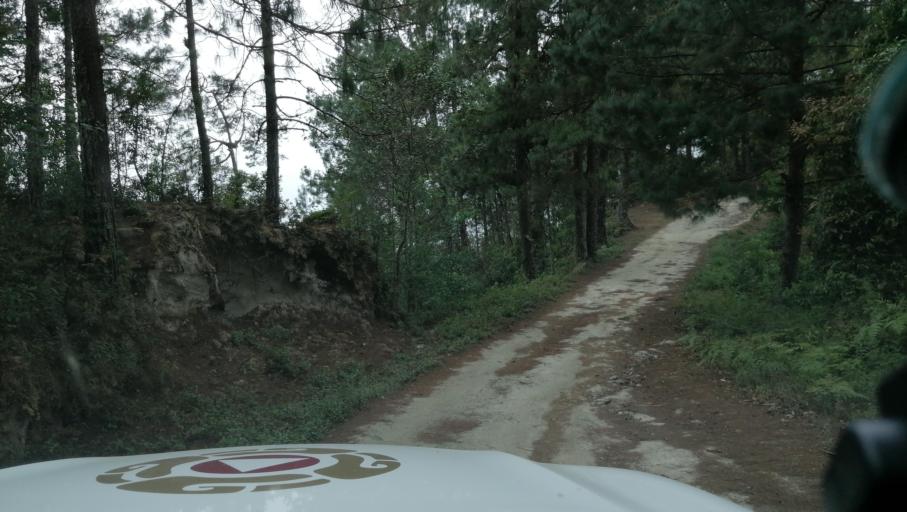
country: MX
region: Chiapas
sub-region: Tapachula
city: Canton Villaflor
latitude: 15.2032
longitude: -92.2364
